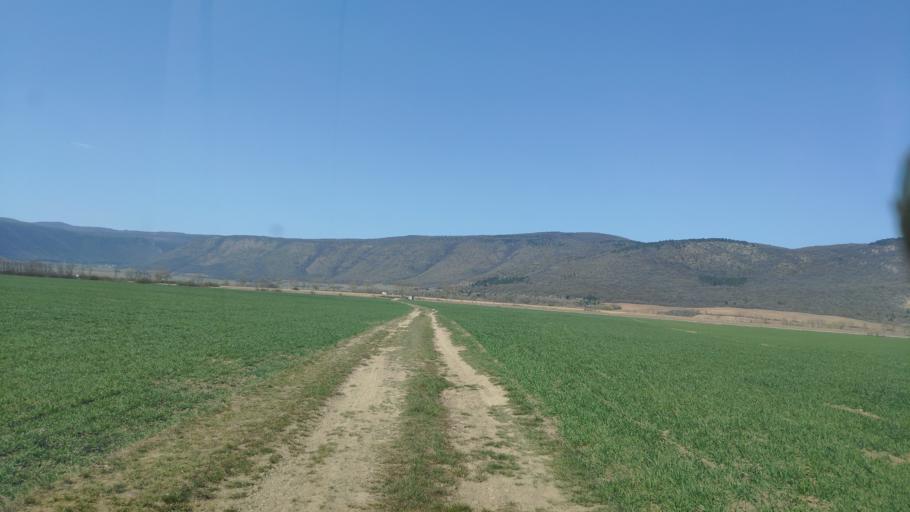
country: SK
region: Kosicky
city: Moldava nad Bodvou
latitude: 48.6013
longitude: 20.9307
